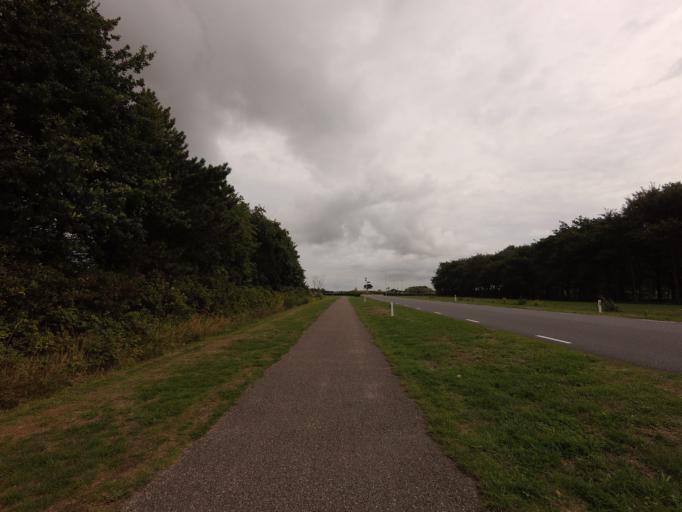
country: NL
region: Friesland
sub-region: Gemeente Ameland
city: Hollum
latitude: 53.4460
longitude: 5.6386
